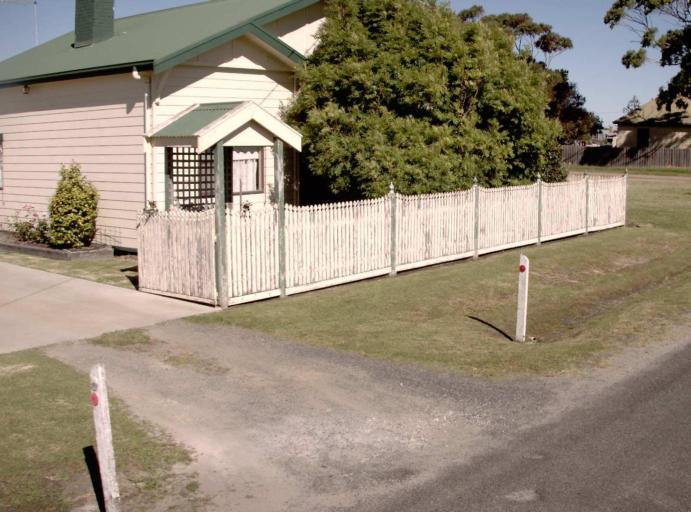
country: AU
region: Victoria
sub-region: Latrobe
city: Traralgon
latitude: -38.6703
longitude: 146.6919
